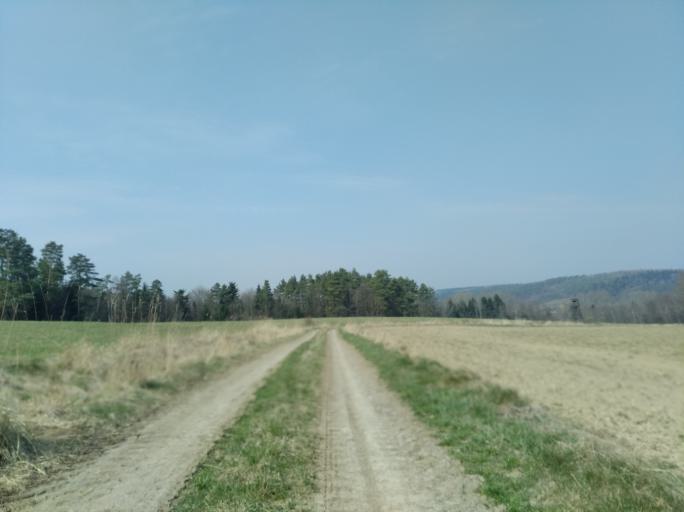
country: PL
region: Subcarpathian Voivodeship
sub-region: Powiat krosnienski
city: Korczyna
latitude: 49.7909
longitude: 21.8074
